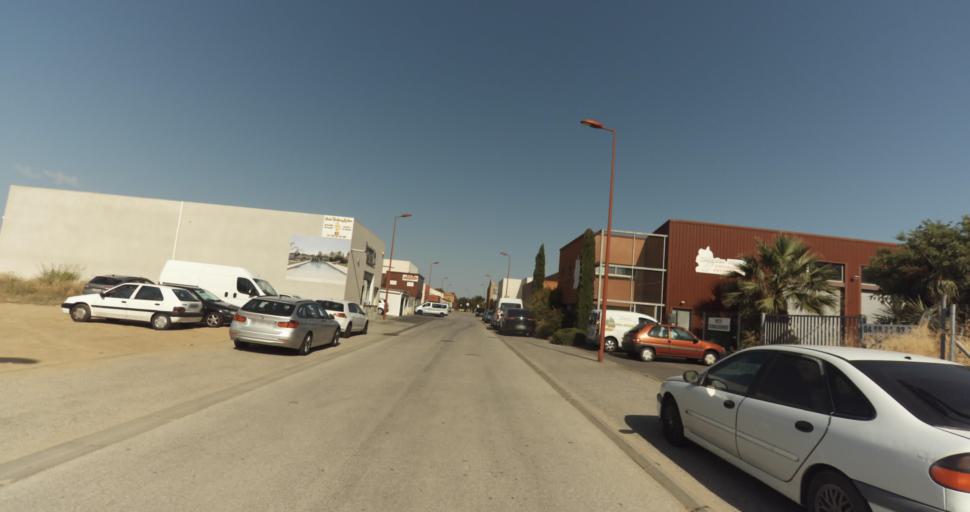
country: FR
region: Languedoc-Roussillon
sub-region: Departement des Pyrenees-Orientales
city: Alenya
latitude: 42.6358
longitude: 2.9862
